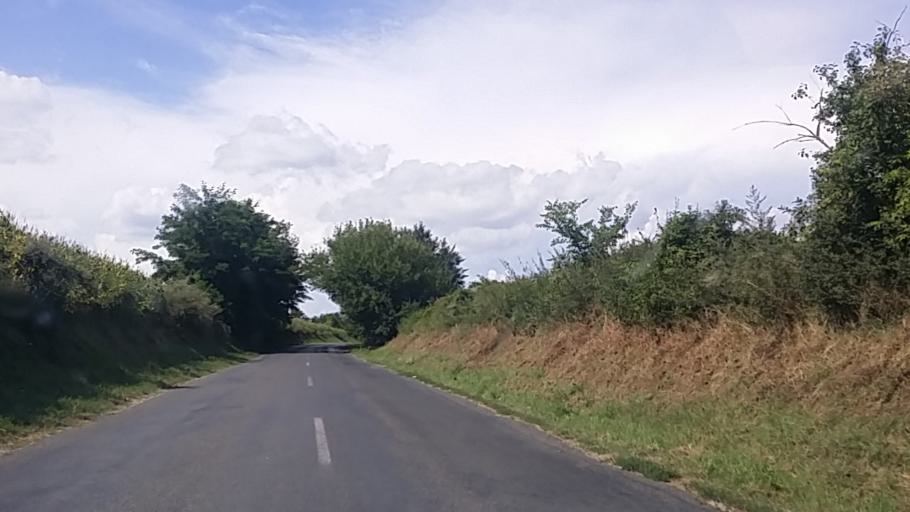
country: HU
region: Tolna
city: Hogyesz
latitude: 46.5126
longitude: 18.4058
